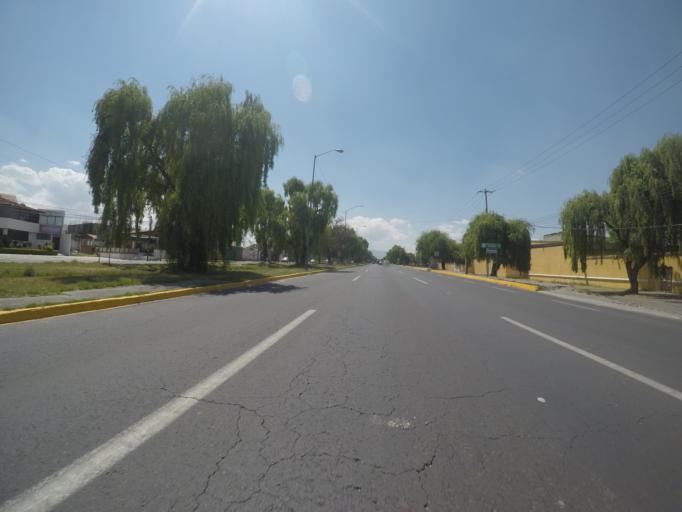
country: MX
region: Mexico
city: Cacalomacan
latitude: 19.2567
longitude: -99.6961
